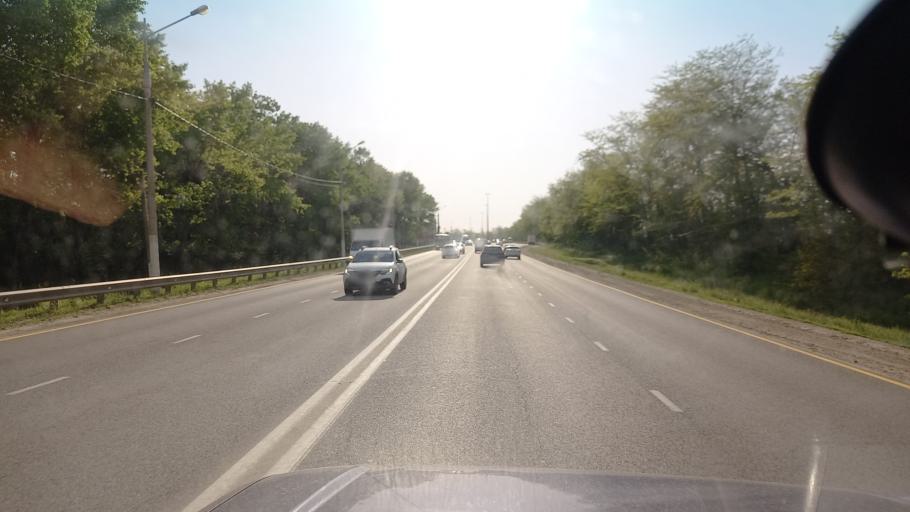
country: RU
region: Krasnodarskiy
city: Yelizavetinskaya
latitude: 45.0567
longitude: 38.8738
